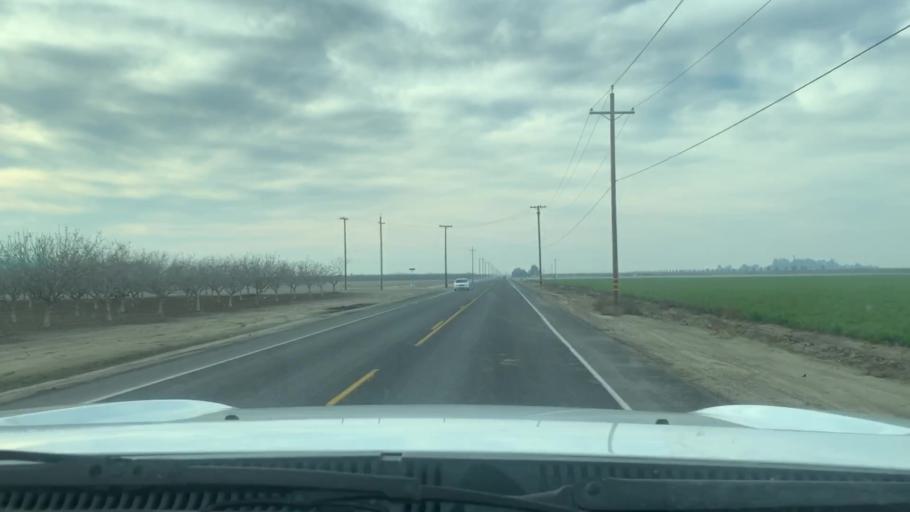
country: US
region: California
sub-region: Kern County
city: Buttonwillow
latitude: 35.4422
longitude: -119.4104
